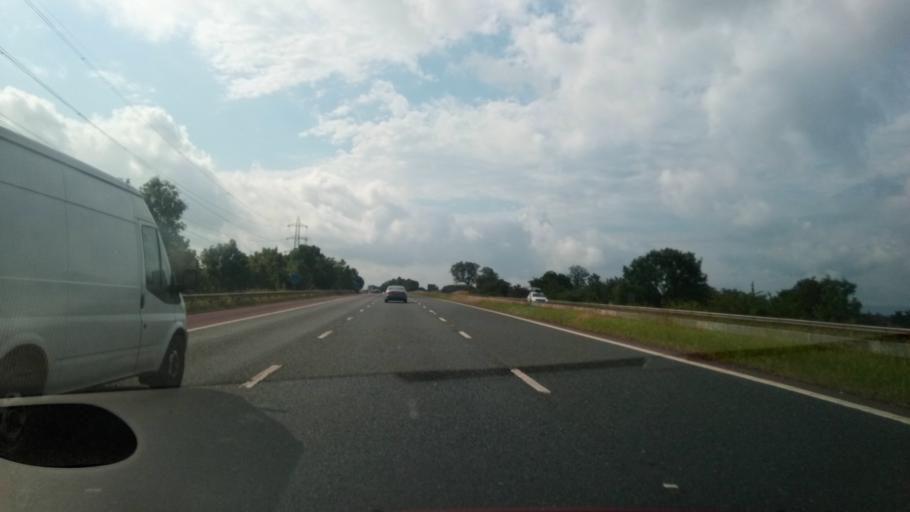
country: GB
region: England
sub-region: Cumbria
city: Scotby
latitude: 54.8874
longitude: -2.8848
